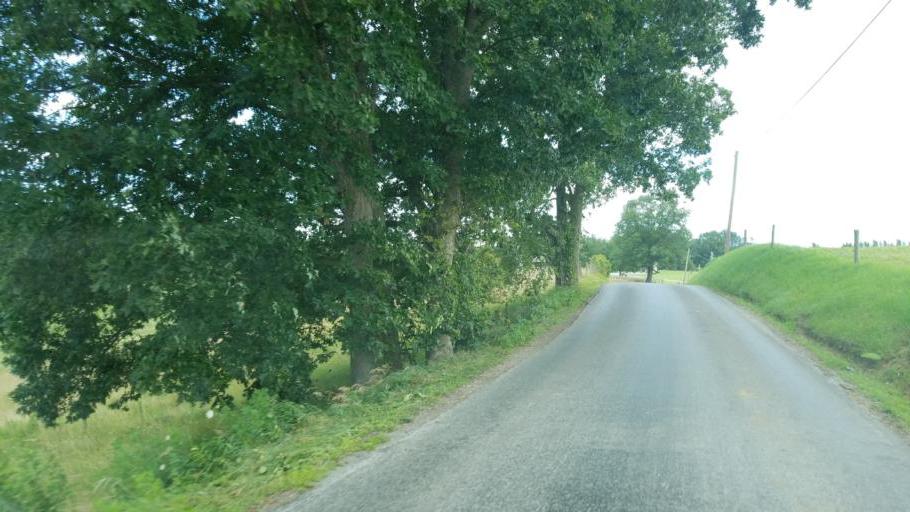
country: US
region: Ohio
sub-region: Holmes County
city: Millersburg
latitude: 40.5029
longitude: -81.8002
